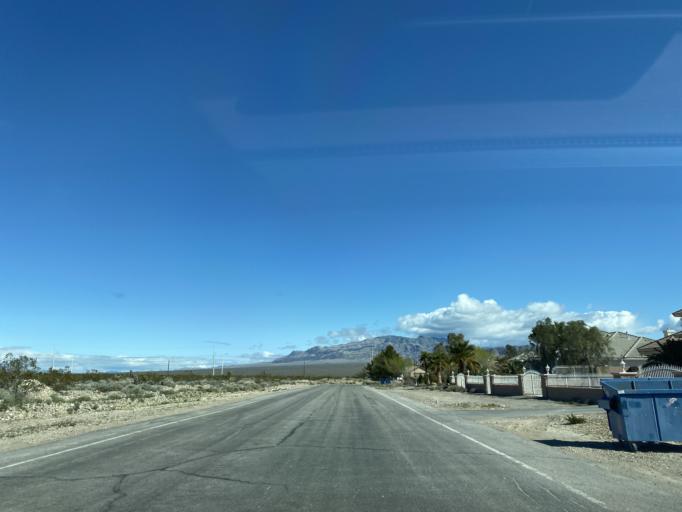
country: US
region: Nevada
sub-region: Clark County
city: North Las Vegas
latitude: 36.3294
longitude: -115.2877
